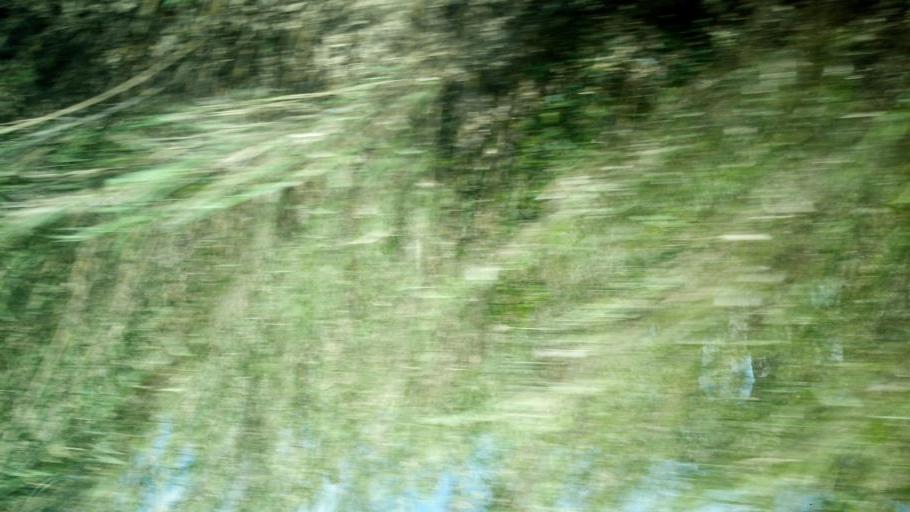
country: IT
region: Latium
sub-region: Citta metropolitana di Roma Capitale
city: Rome
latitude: 41.8533
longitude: 12.5515
